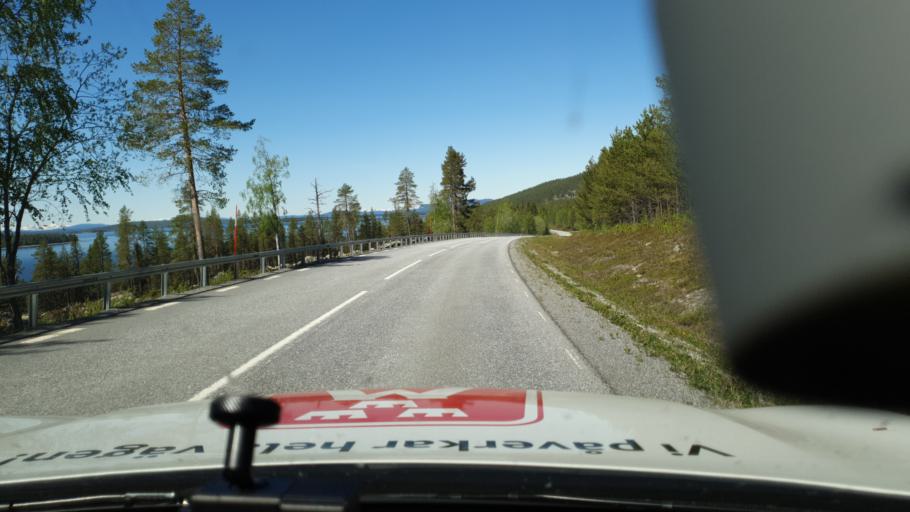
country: SE
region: Vaesterbotten
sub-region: Storumans Kommun
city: Storuman
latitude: 65.1471
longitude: 17.0769
